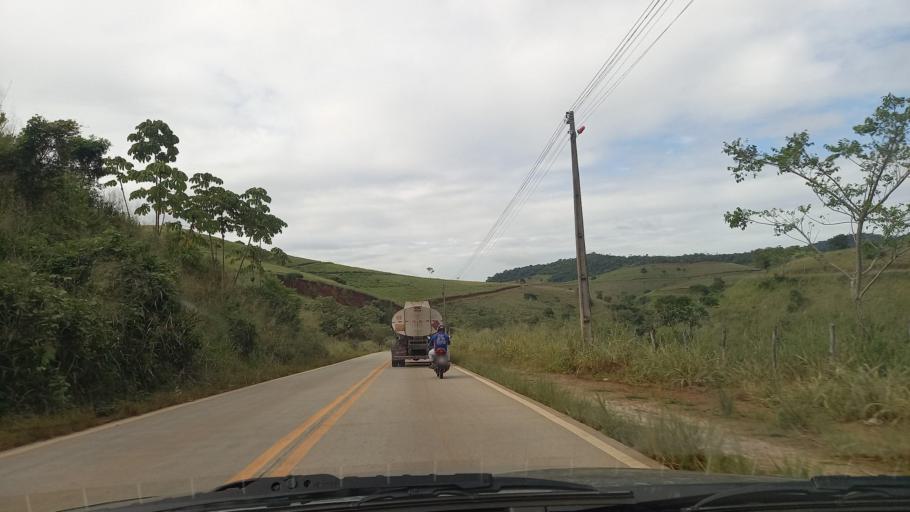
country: BR
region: Pernambuco
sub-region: Maraial
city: Maraial
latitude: -8.7487
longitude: -35.8068
